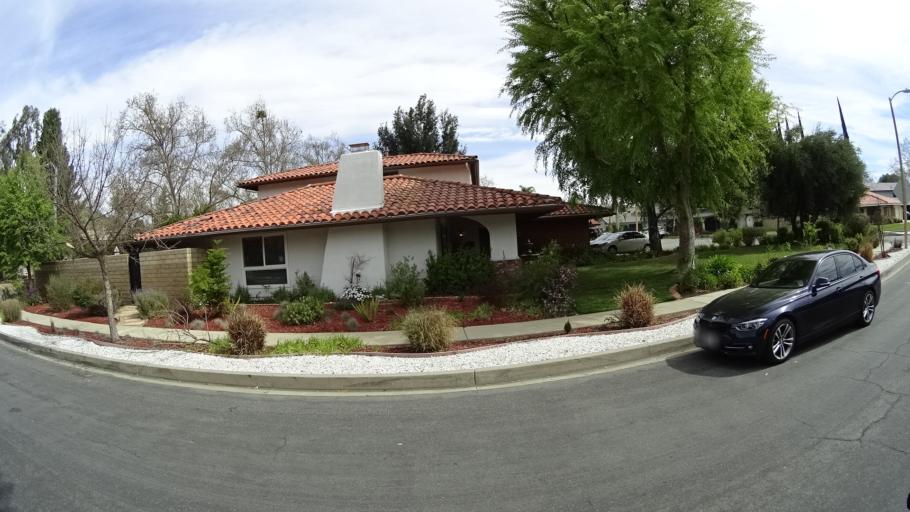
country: US
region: California
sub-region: Ventura County
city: Thousand Oaks
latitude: 34.1468
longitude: -118.8425
